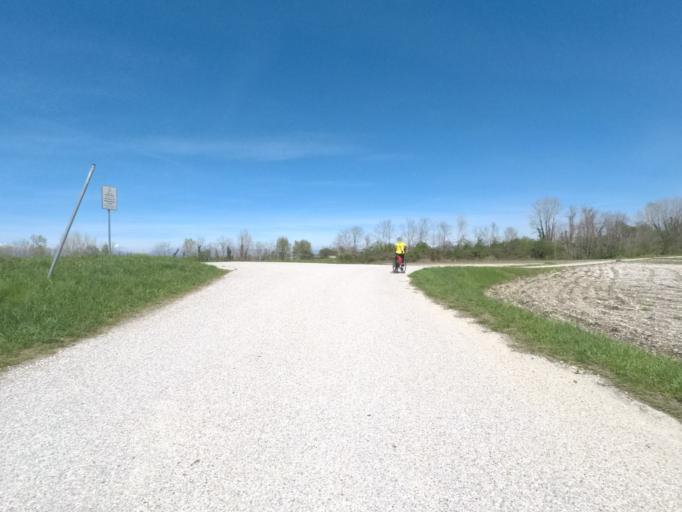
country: IT
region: Friuli Venezia Giulia
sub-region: Provincia di Udine
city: Camino al Tagliamento
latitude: 45.9582
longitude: 12.9127
